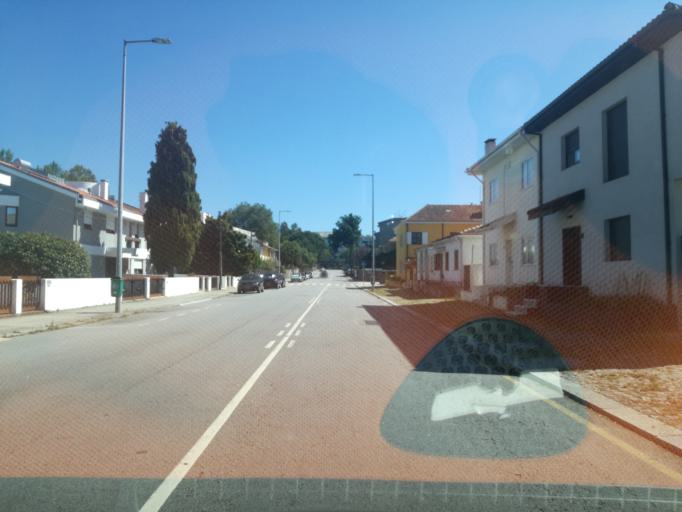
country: PT
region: Porto
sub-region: Matosinhos
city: Sao Mamede de Infesta
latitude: 41.1802
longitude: -8.6093
